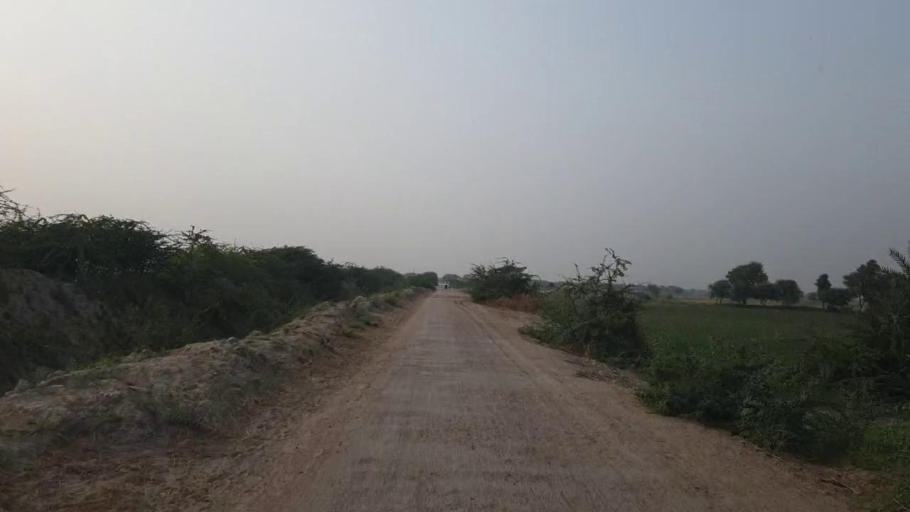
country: PK
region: Sindh
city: Mirpur Batoro
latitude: 24.6470
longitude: 68.3921
